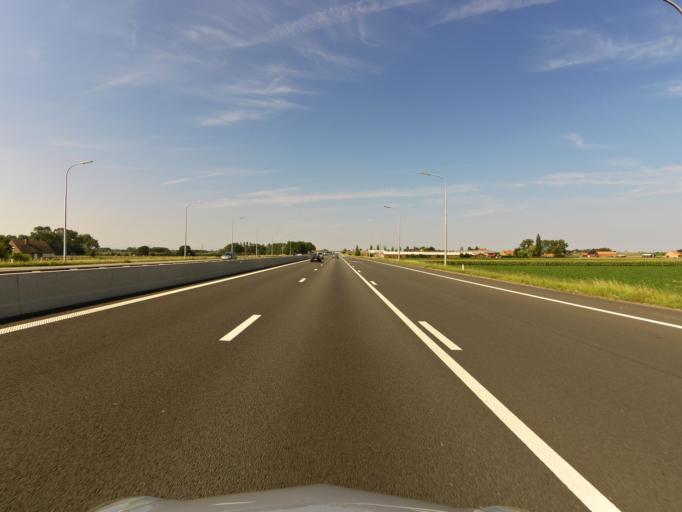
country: BE
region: Flanders
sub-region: Provincie West-Vlaanderen
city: Lichtervelde
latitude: 51.0129
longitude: 3.1702
